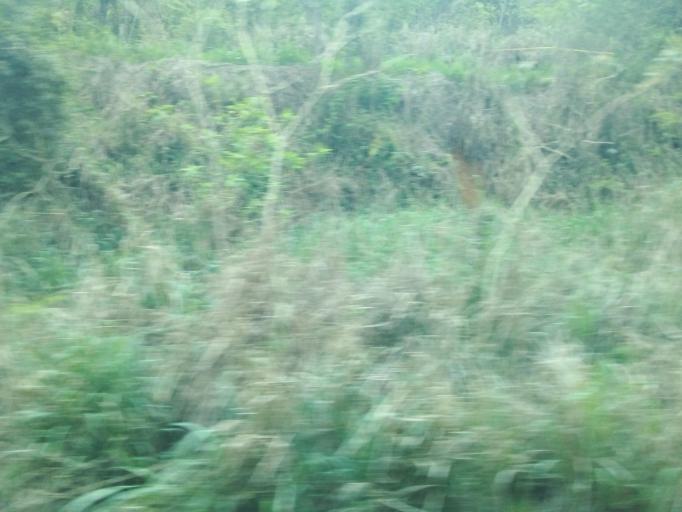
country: BR
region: Minas Gerais
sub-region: Ipaba
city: Ipaba
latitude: -19.4631
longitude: -42.4528
